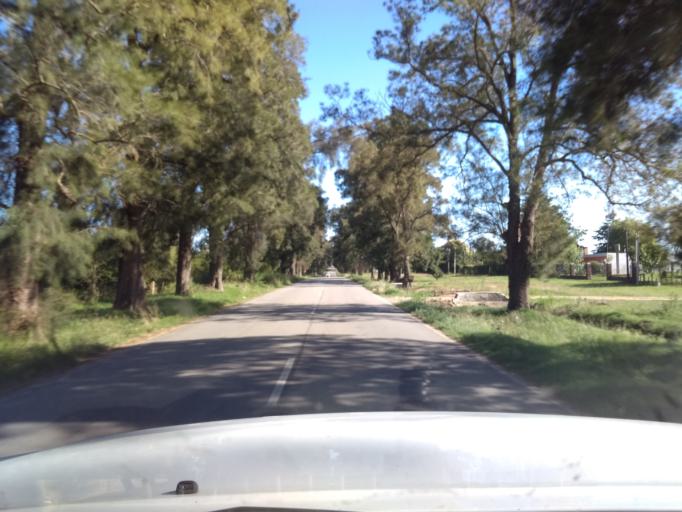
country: UY
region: Canelones
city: San Bautista
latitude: -34.3762
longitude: -55.9595
